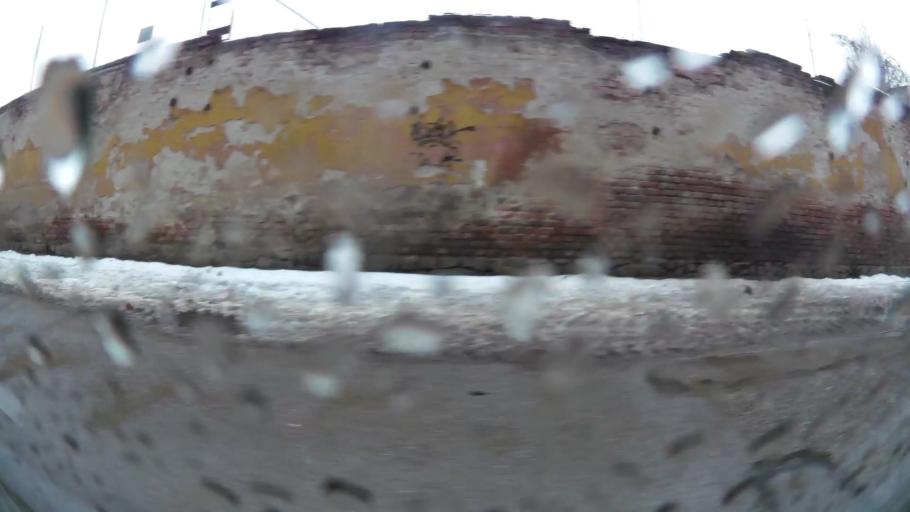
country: BG
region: Sofia-Capital
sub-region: Stolichna Obshtina
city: Sofia
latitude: 42.6781
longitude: 23.2786
